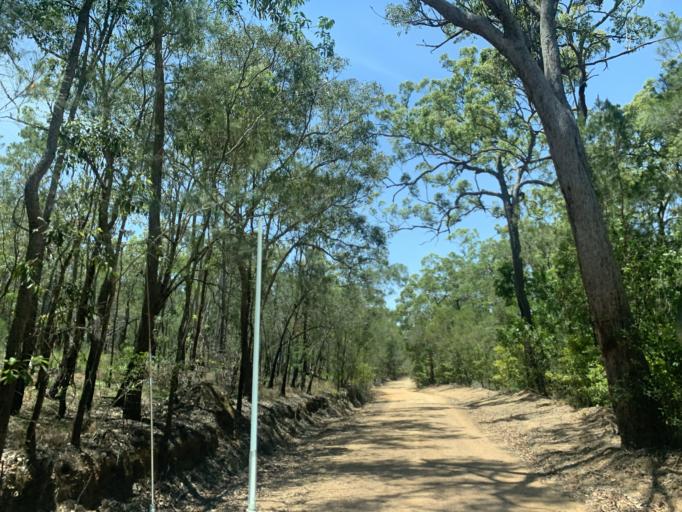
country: AU
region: Queensland
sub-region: Cairns
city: Redlynch
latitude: -16.9278
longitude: 145.6029
